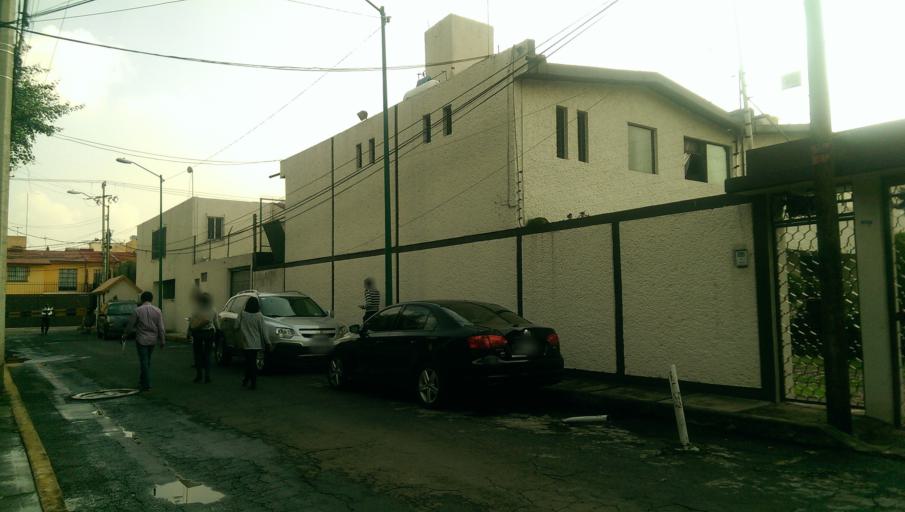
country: MX
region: Mexico City
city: Tlalpan
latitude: 19.2890
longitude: -99.1376
